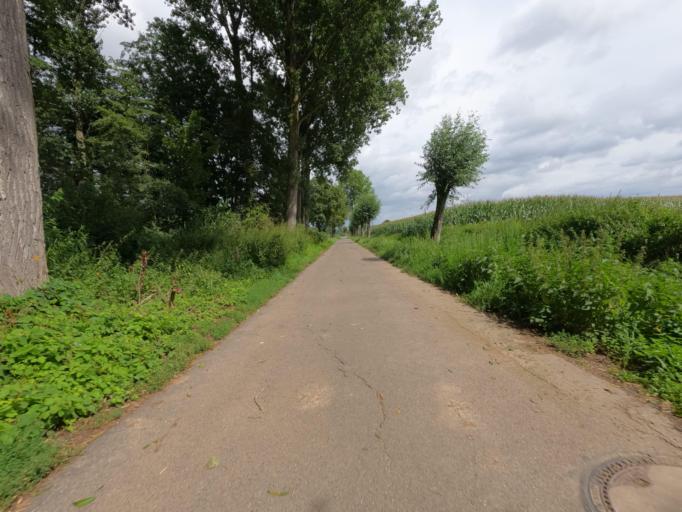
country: DE
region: North Rhine-Westphalia
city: Huckelhoven
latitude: 51.0244
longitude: 6.1797
